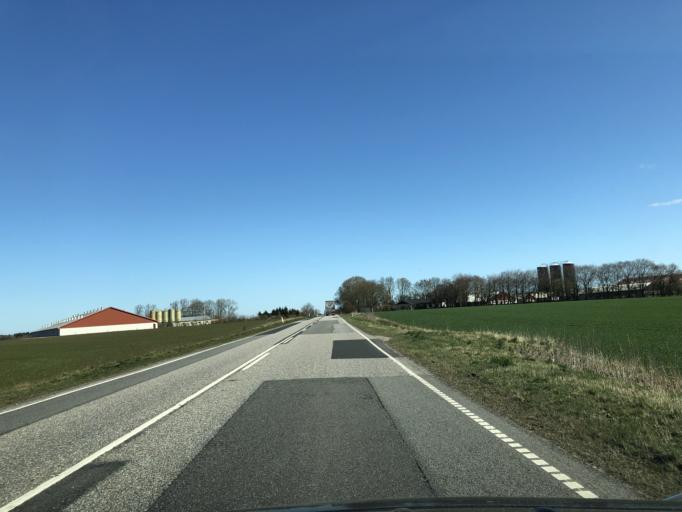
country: DK
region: North Denmark
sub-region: Rebild Kommune
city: Stovring
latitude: 56.8534
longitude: 9.8245
